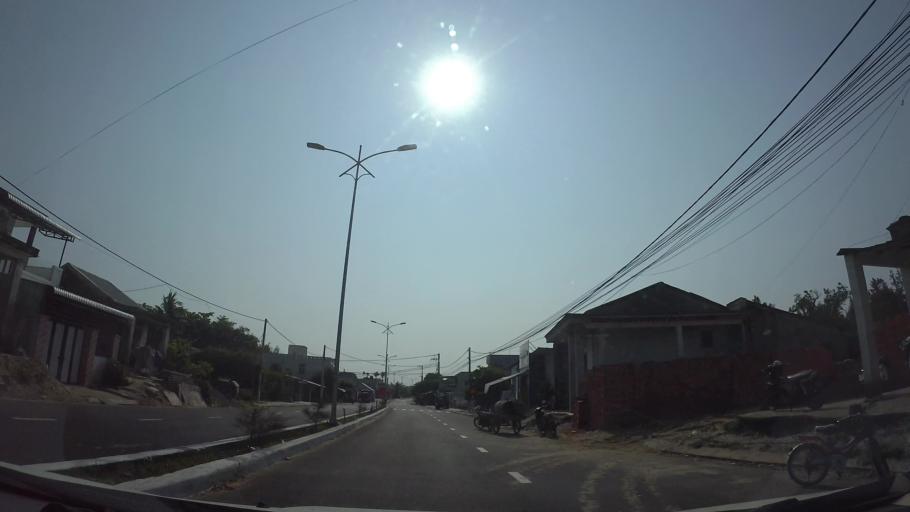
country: VN
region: Da Nang
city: Ngu Hanh Son
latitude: 15.9562
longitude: 108.2878
